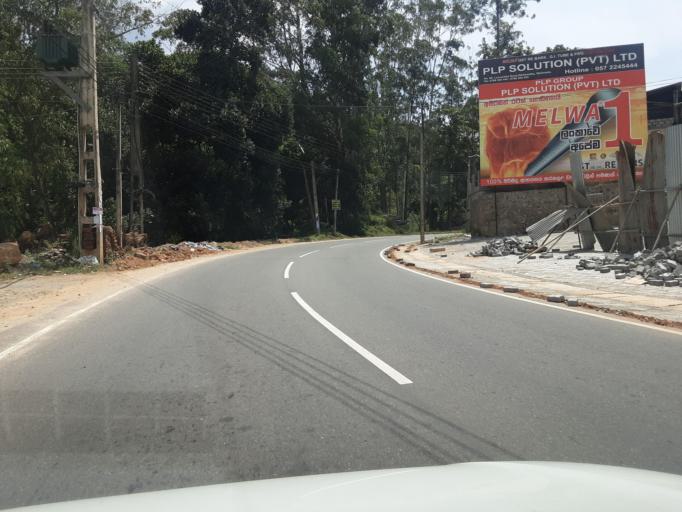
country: LK
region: Central
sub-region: Nuwara Eliya District
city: Nuwara Eliya
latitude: 6.9112
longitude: 80.9060
